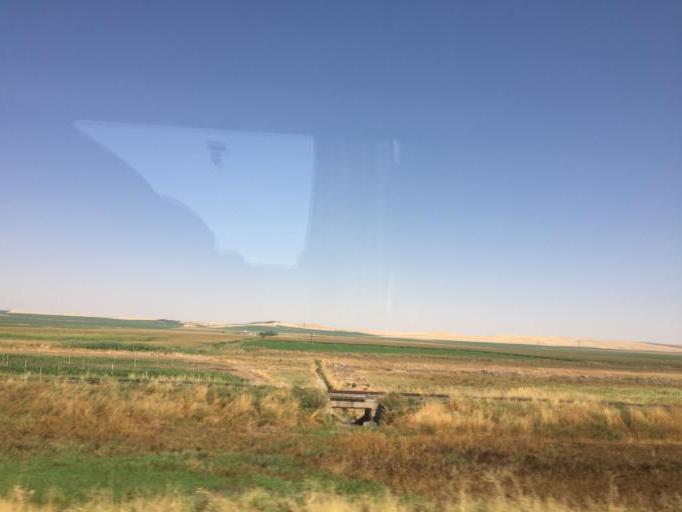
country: TR
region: Diyarbakir
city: Tepe
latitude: 37.8499
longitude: 40.7816
